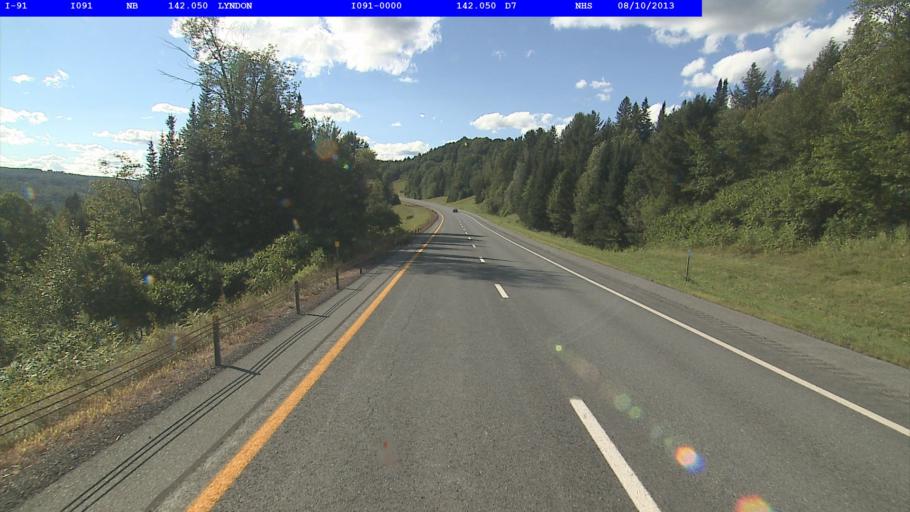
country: US
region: Vermont
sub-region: Caledonia County
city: Lyndonville
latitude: 44.5781
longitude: -72.0496
